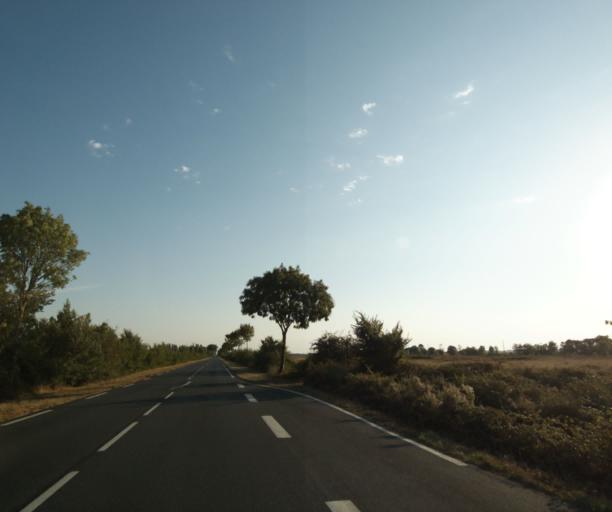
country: FR
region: Poitou-Charentes
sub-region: Departement de la Charente-Maritime
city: Tonnay-Charente
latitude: 45.9609
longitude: -0.9294
